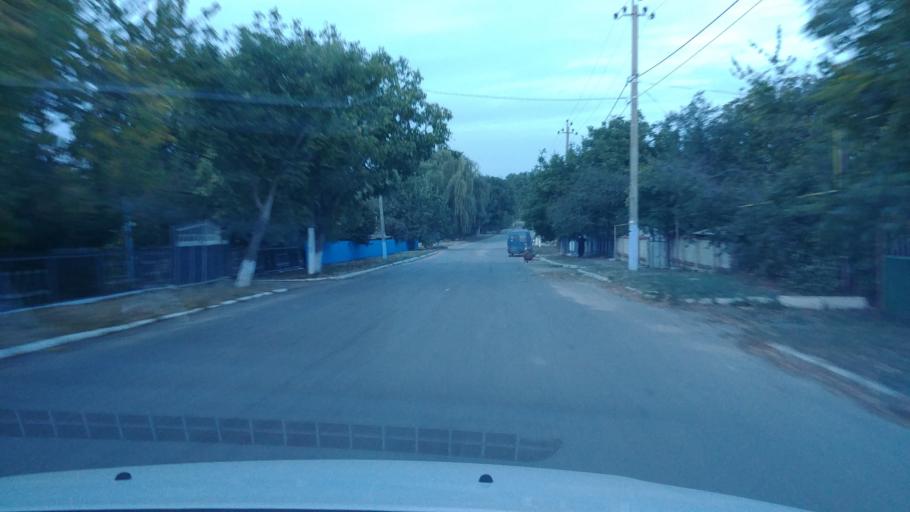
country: MD
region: Rezina
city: Saharna
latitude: 47.6751
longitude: 28.9588
